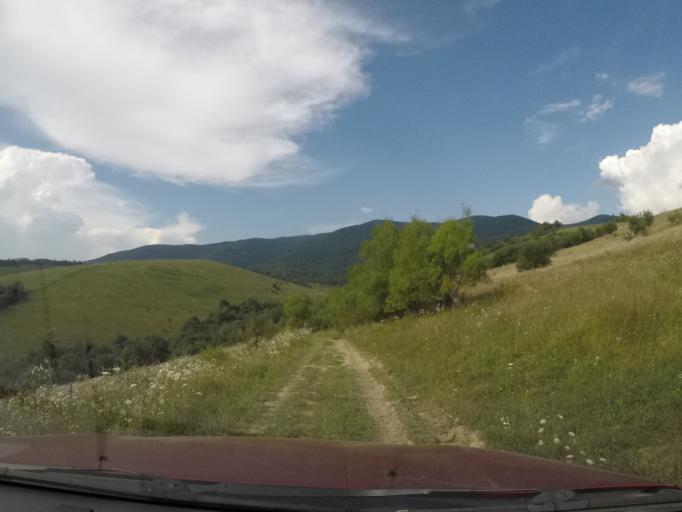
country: UA
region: Zakarpattia
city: Velykyi Bereznyi
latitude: 49.0256
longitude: 22.6364
